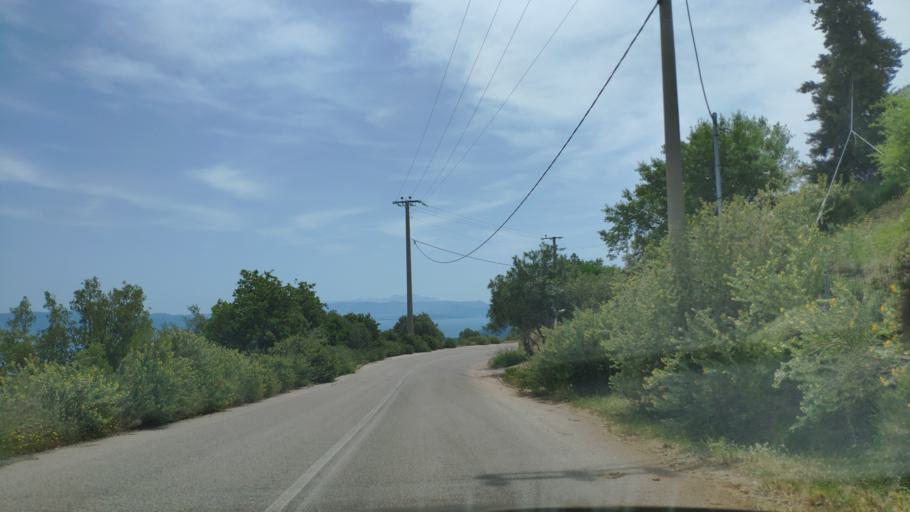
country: GR
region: Attica
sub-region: Nomarchia Anatolikis Attikis
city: Grammatiko
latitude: 38.2527
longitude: 23.9669
